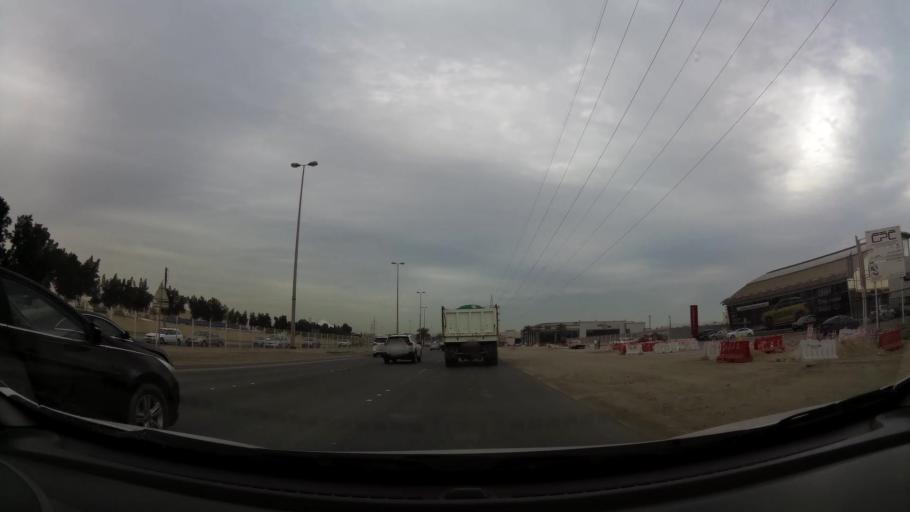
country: BH
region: Northern
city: Sitrah
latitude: 26.1665
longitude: 50.6044
